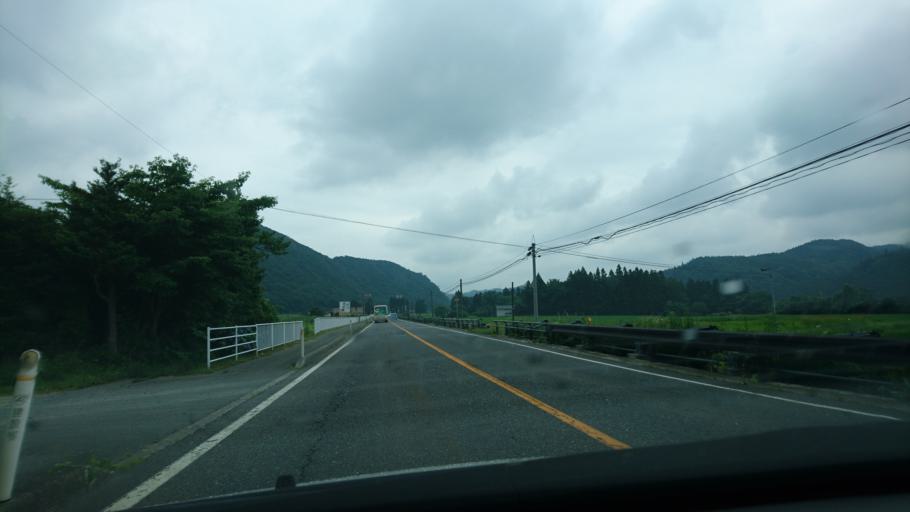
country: JP
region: Miyagi
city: Furukawa
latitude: 38.7293
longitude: 140.7941
